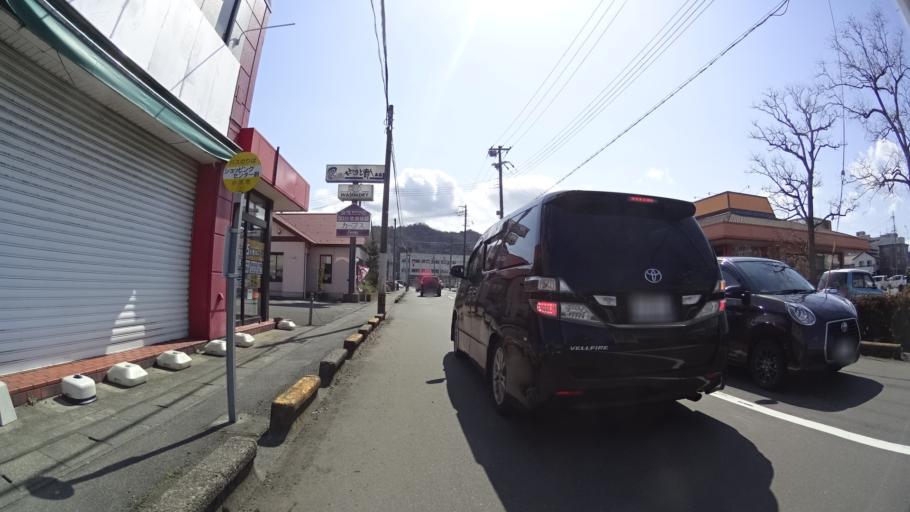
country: JP
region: Fukui
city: Obama
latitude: 35.4963
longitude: 135.7499
